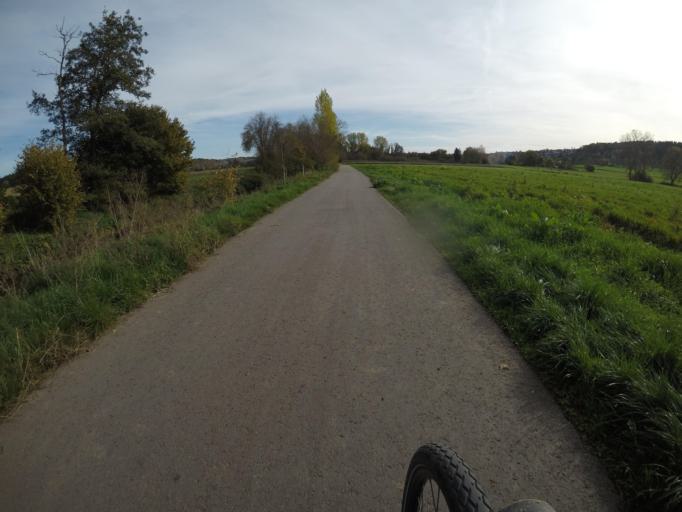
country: DE
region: Baden-Wuerttemberg
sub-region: Regierungsbezirk Stuttgart
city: Weil der Stadt
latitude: 48.7649
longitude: 8.8599
